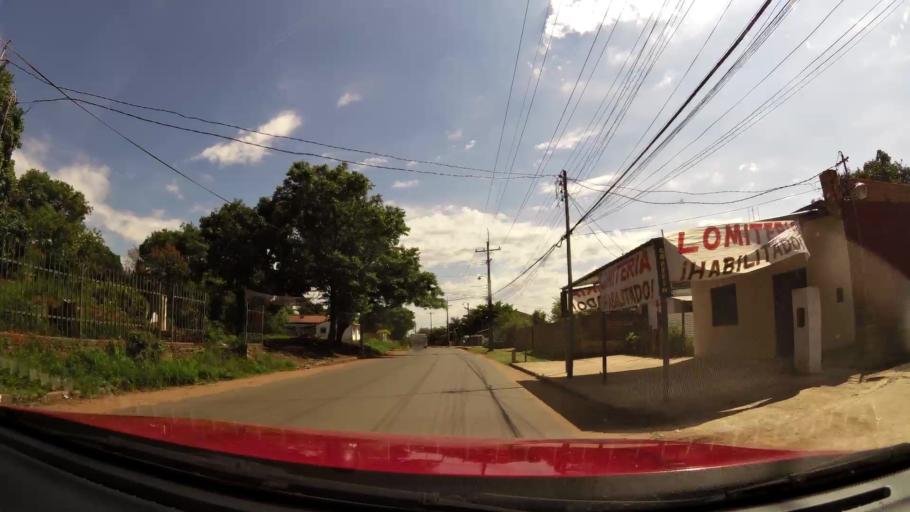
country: PY
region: Central
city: San Lorenzo
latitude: -25.2557
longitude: -57.4936
